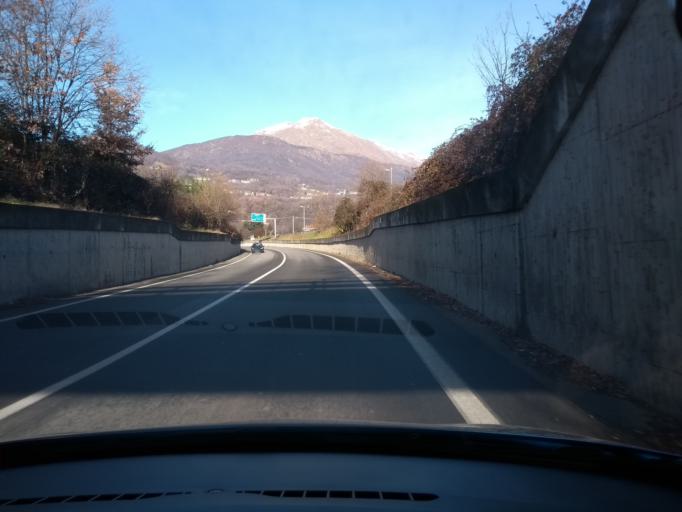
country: IT
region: Piedmont
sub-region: Provincia di Torino
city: Cuorgne
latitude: 45.3985
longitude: 7.6600
